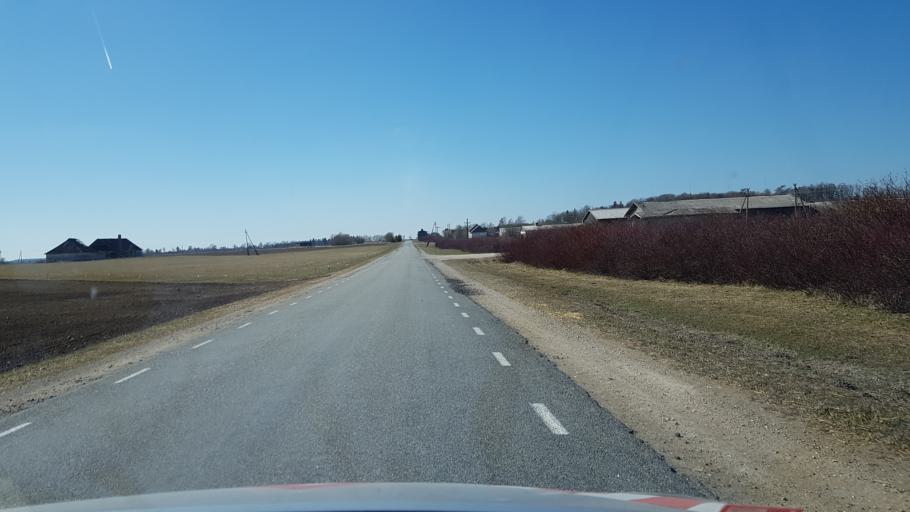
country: EE
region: Laeaene-Virumaa
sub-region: Vaeike-Maarja vald
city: Vaike-Maarja
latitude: 59.1134
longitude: 26.3483
